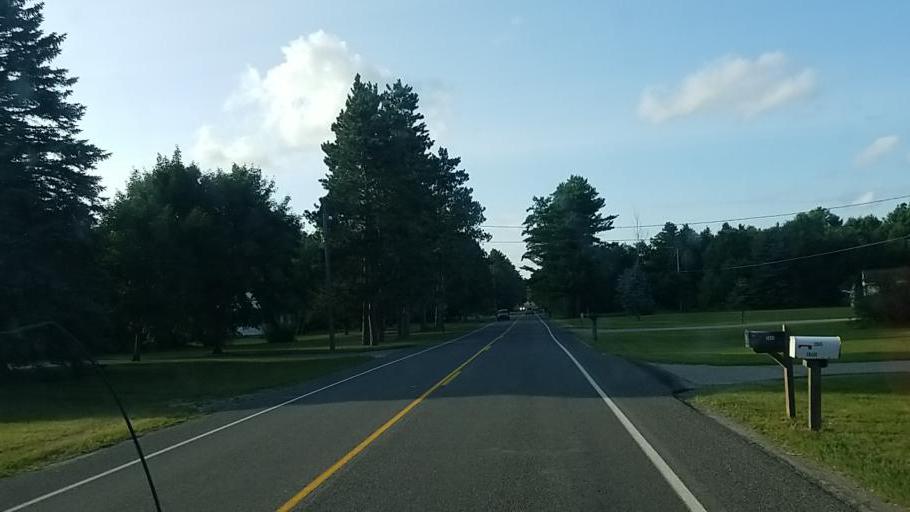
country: US
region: Michigan
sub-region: Montcalm County
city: Greenville
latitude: 43.1995
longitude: -85.3519
